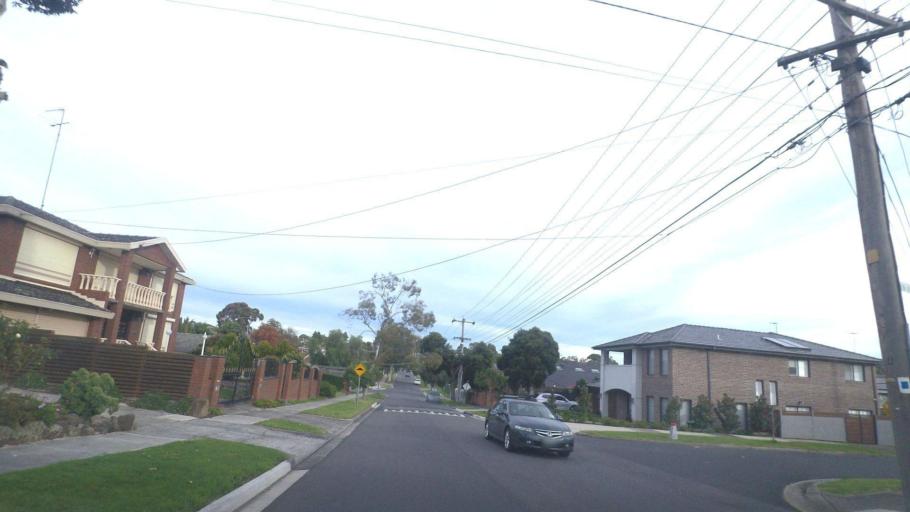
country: AU
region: Victoria
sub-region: Manningham
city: Bulleen
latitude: -37.7721
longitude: 145.0869
